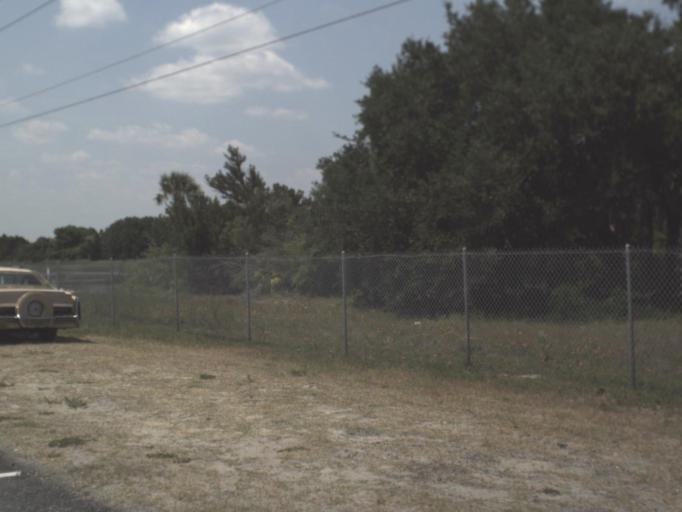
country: US
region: Florida
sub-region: Duval County
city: Atlantic Beach
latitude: 30.3710
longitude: -81.4317
